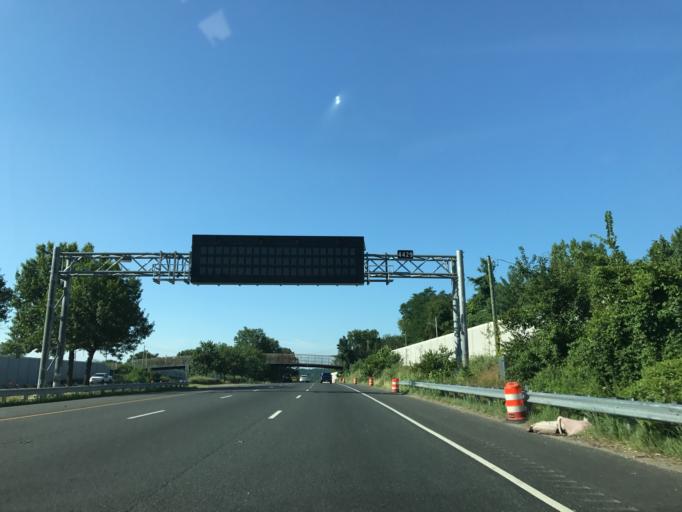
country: US
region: Maryland
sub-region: Baltimore County
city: Lansdowne
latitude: 39.2409
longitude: -76.6489
